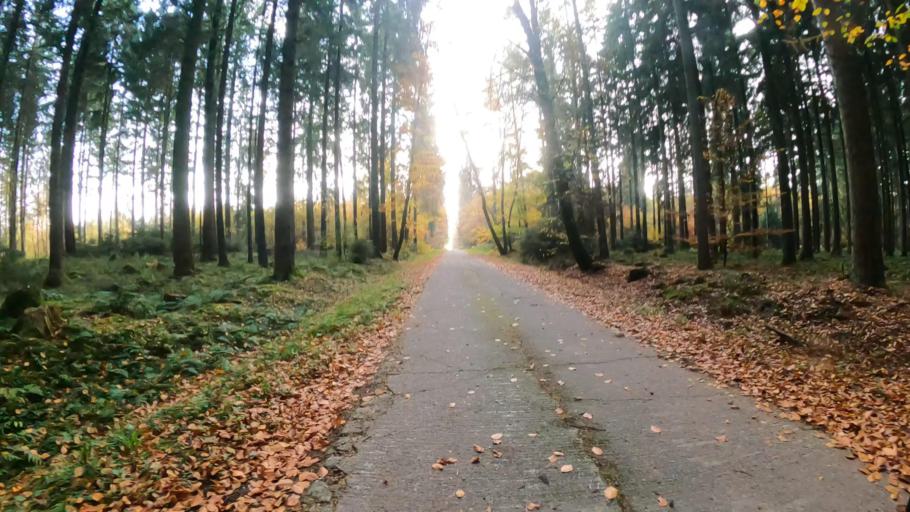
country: DE
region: Lower Saxony
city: Buchholz in der Nordheide
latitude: 53.3507
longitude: 9.8213
